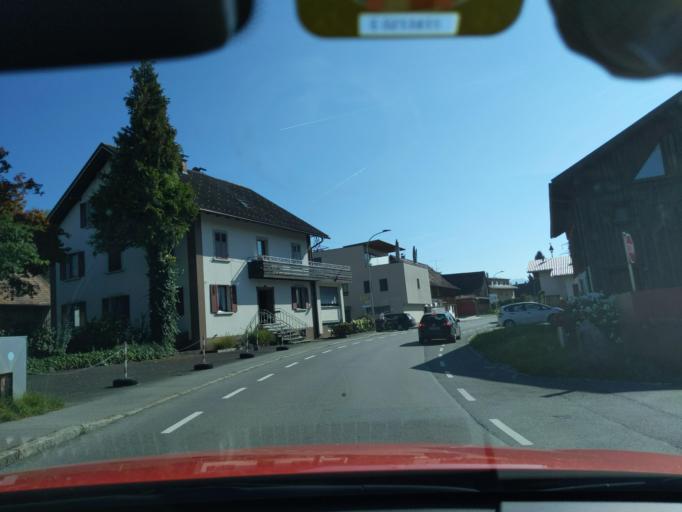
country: AT
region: Vorarlberg
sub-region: Politischer Bezirk Bregenz
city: Horbranz
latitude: 47.5492
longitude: 9.7521
